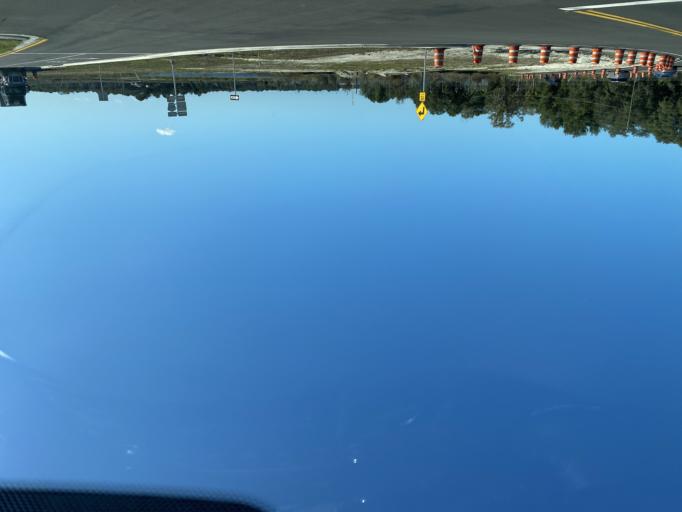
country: US
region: Florida
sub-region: Lake County
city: Mount Plymouth
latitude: 28.8121
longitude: -81.5111
